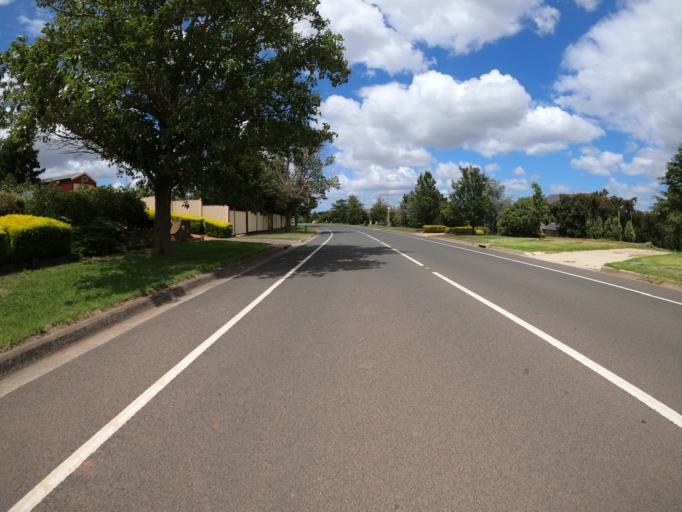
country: AU
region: Victoria
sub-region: Hume
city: Attwood
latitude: -37.6577
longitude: 144.8930
